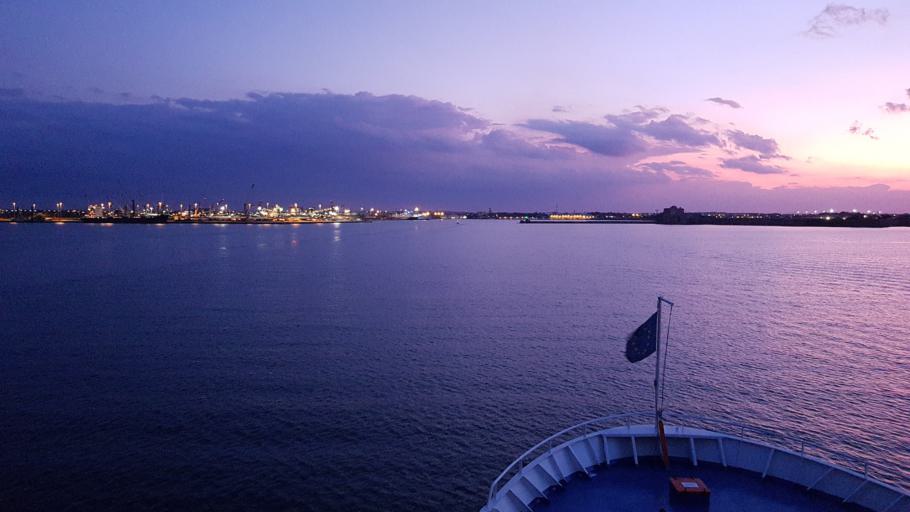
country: IT
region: Apulia
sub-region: Provincia di Brindisi
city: Materdomini
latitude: 40.6580
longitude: 17.9833
